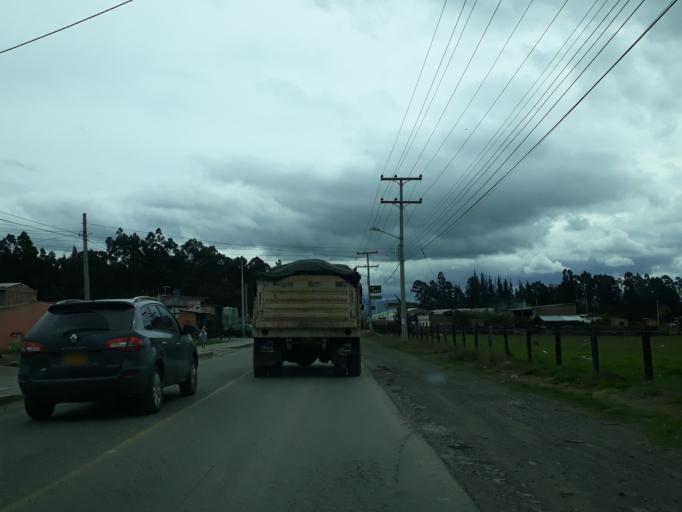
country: CO
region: Cundinamarca
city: Simijaca
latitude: 5.5099
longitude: -73.8455
